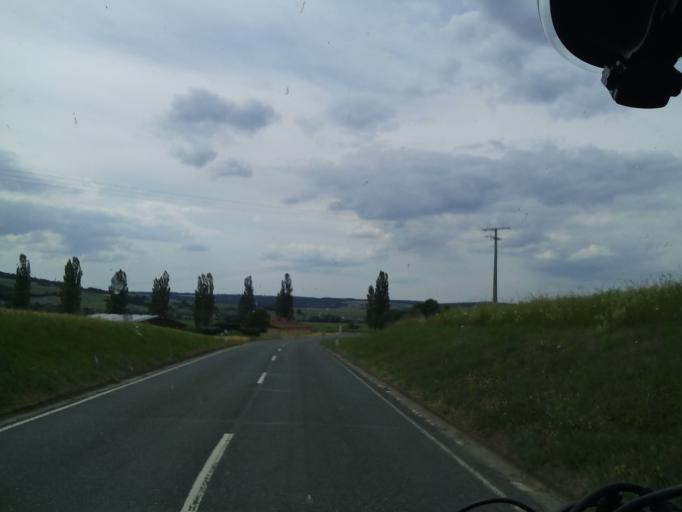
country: DE
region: Bavaria
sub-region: Regierungsbezirk Unterfranken
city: Untermerzbach
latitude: 50.1042
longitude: 10.8721
